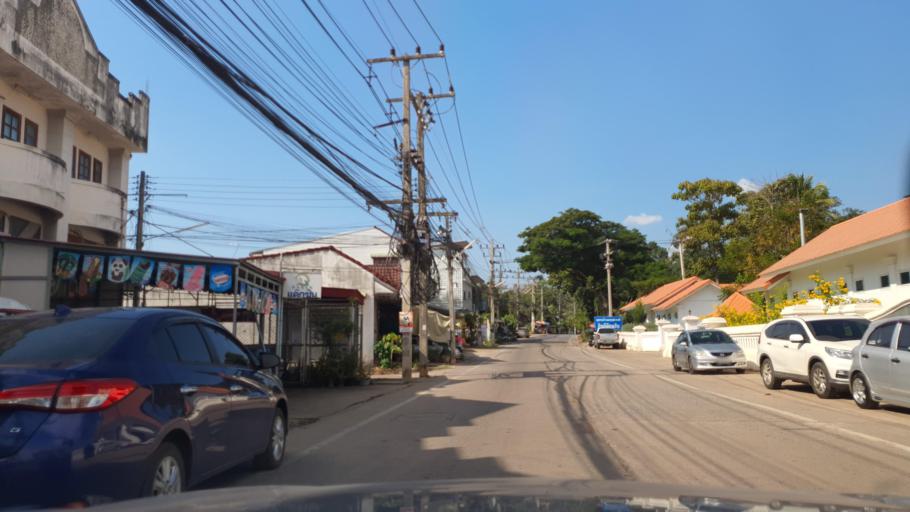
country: TH
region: Nan
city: Nan
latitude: 18.7883
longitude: 100.7754
